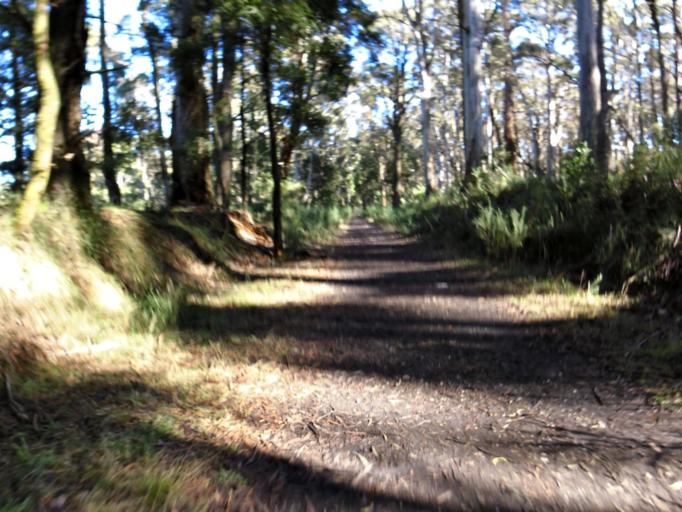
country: AU
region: Victoria
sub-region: Moorabool
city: Bacchus Marsh
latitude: -37.3878
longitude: 144.3050
